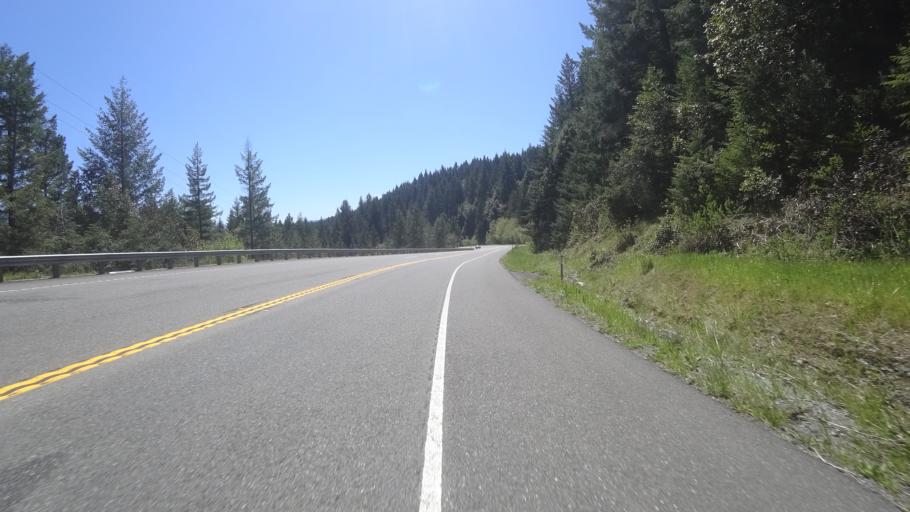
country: US
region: California
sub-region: Humboldt County
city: Blue Lake
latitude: 40.9240
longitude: -123.8366
